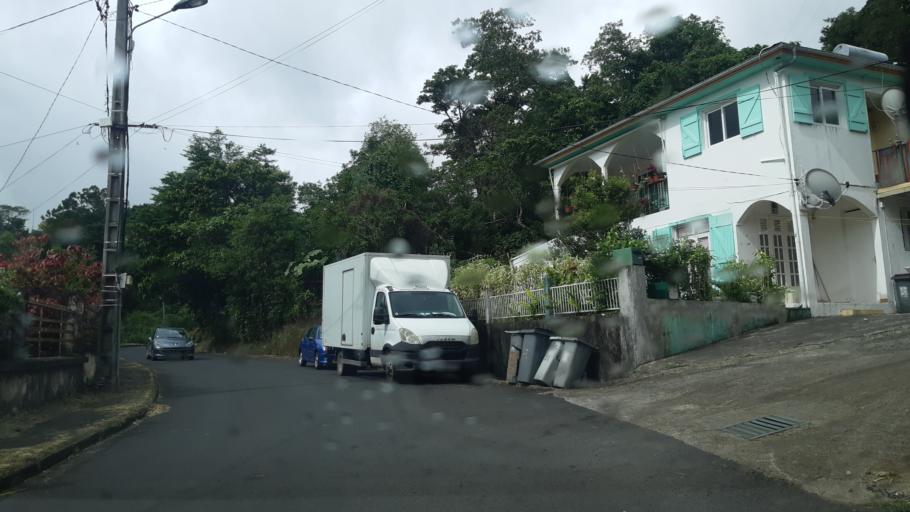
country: GP
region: Guadeloupe
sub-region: Guadeloupe
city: Saint-Claude
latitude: 16.0443
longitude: -61.6926
